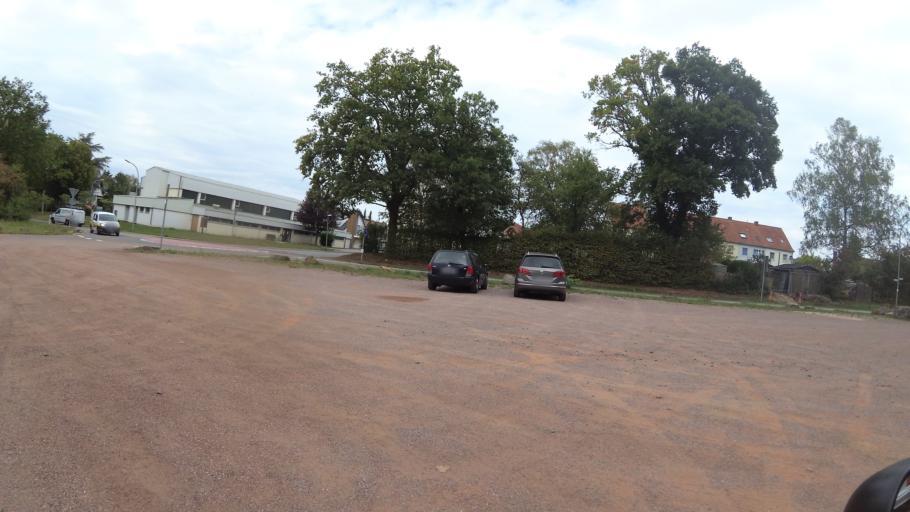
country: FR
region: Lorraine
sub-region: Departement de la Moselle
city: Sarreguemines
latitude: 49.1313
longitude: 7.0705
